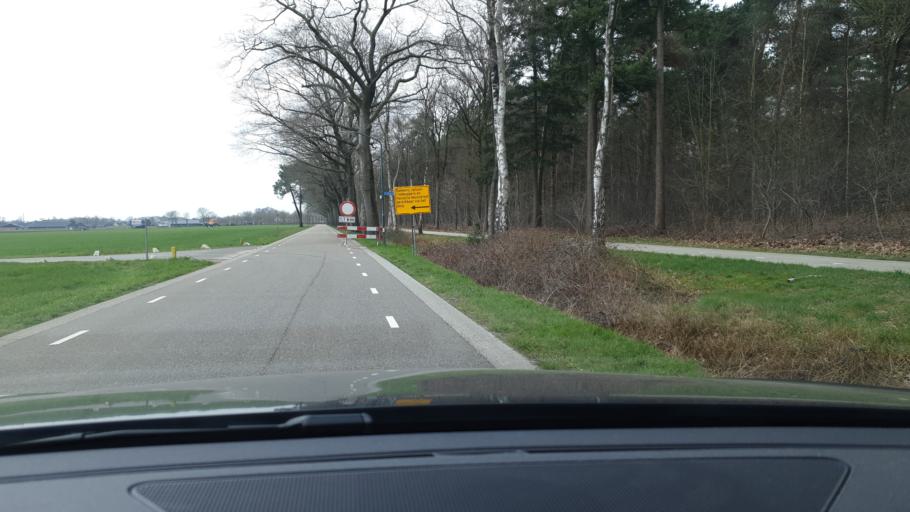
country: NL
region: North Brabant
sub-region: Gemeente Oirschot
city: Middelbeers
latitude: 51.4094
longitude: 5.2743
